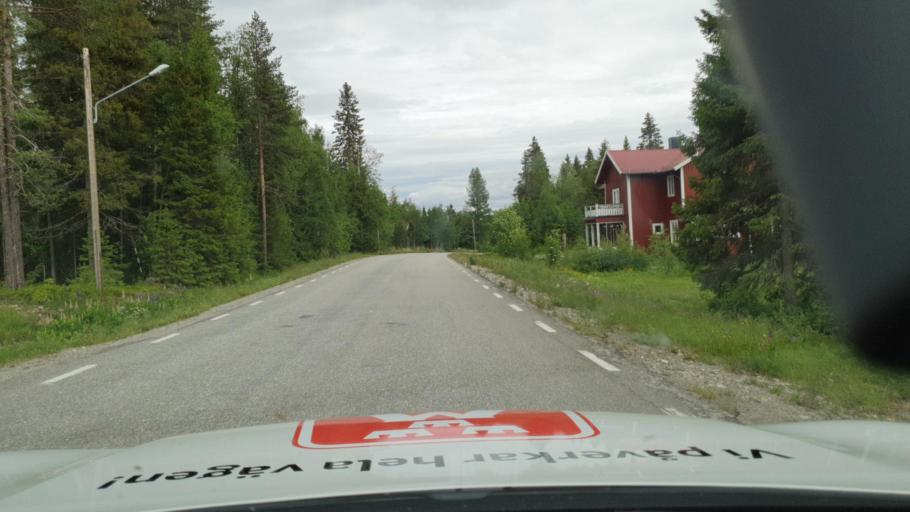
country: SE
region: Vaesterbotten
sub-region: Lycksele Kommun
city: Soderfors
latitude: 64.3599
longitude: 18.1157
